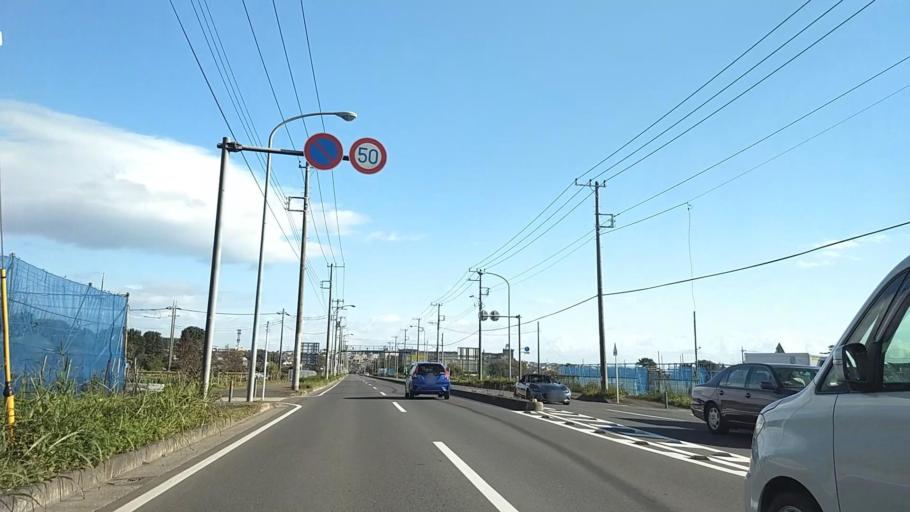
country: JP
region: Tokyo
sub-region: Machida-shi
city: Machida
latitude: 35.5597
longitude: 139.5250
